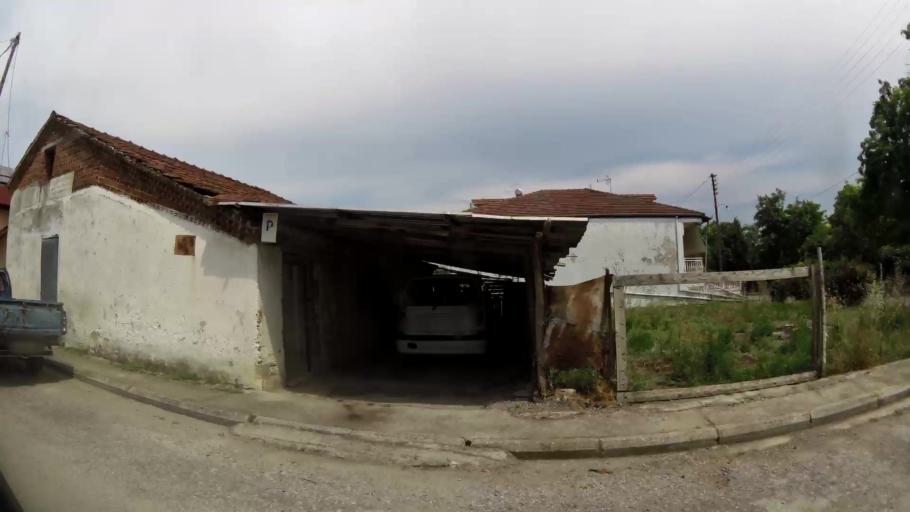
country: GR
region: Central Macedonia
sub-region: Nomos Pierias
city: Korinos
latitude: 40.3129
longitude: 22.5764
